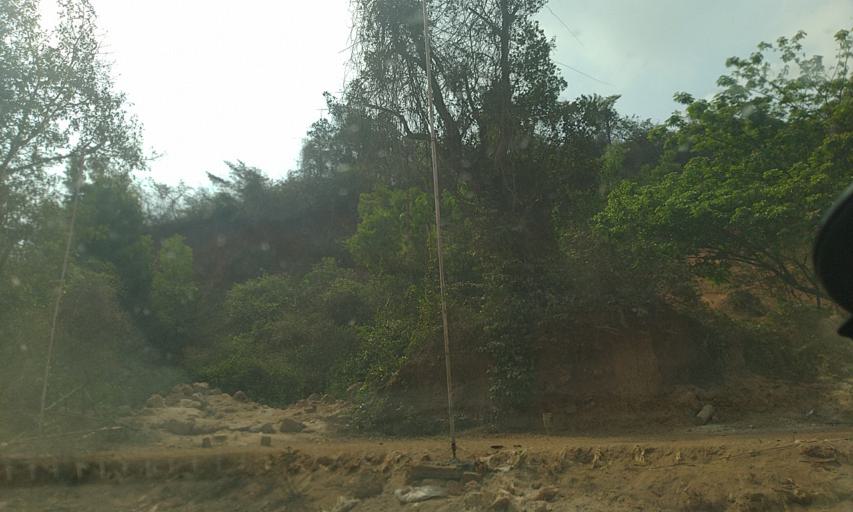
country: IN
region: Goa
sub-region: North Goa
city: Taleigao
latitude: 15.4656
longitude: 73.8274
